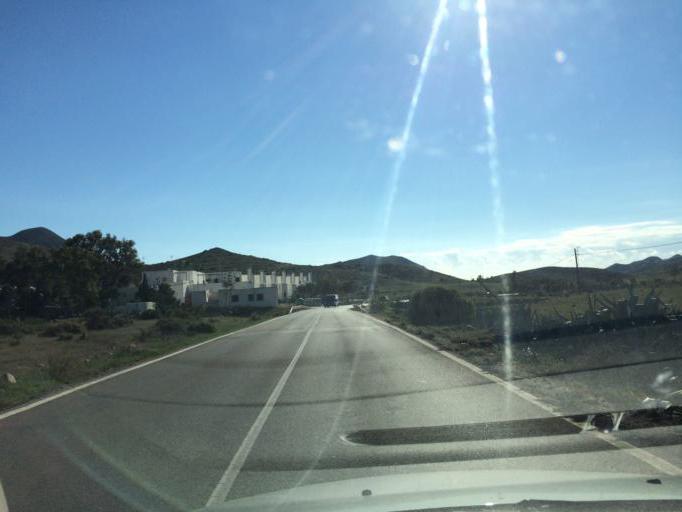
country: ES
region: Andalusia
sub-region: Provincia de Almeria
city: San Jose
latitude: 36.7887
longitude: -2.1094
